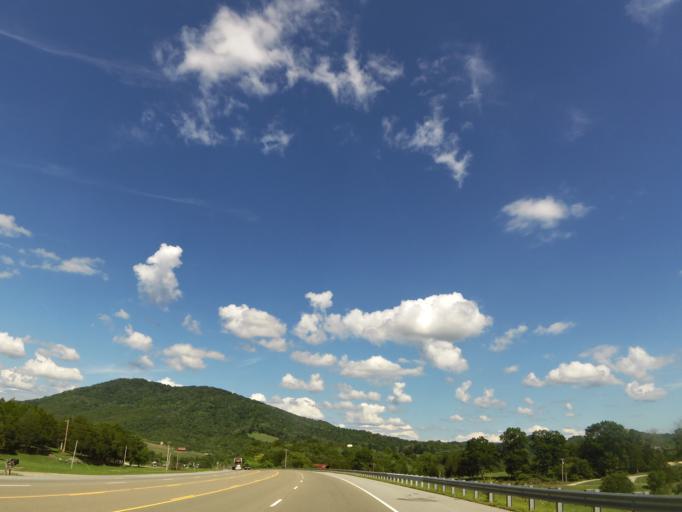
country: US
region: Tennessee
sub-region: Claiborne County
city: Tazewell
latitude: 36.4218
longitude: -83.5347
